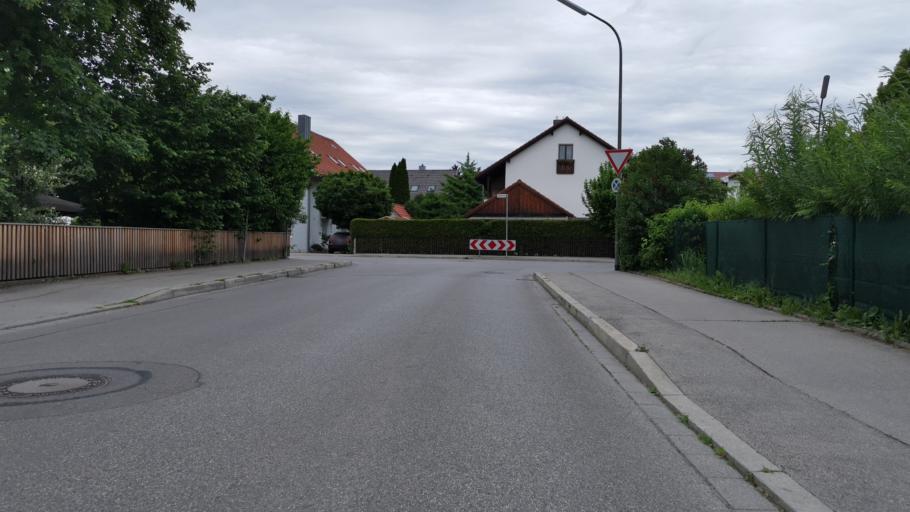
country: DE
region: Bavaria
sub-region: Upper Bavaria
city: Puchheim
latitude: 48.1275
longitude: 11.3542
